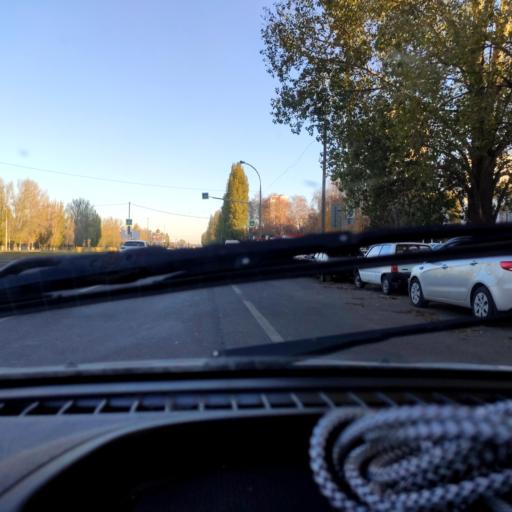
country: RU
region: Samara
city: Tol'yatti
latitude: 53.5084
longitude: 49.2769
